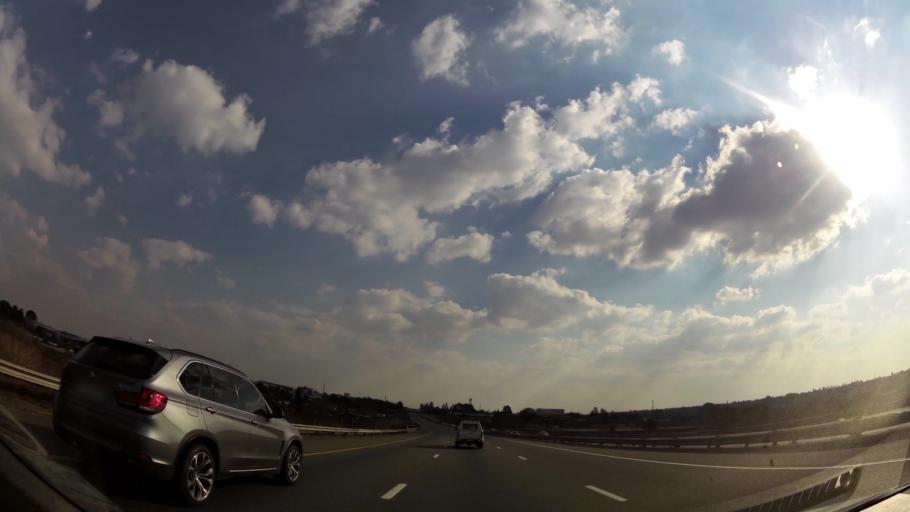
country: ZA
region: Gauteng
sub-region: Ekurhuleni Metropolitan Municipality
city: Germiston
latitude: -26.2519
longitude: 28.2059
